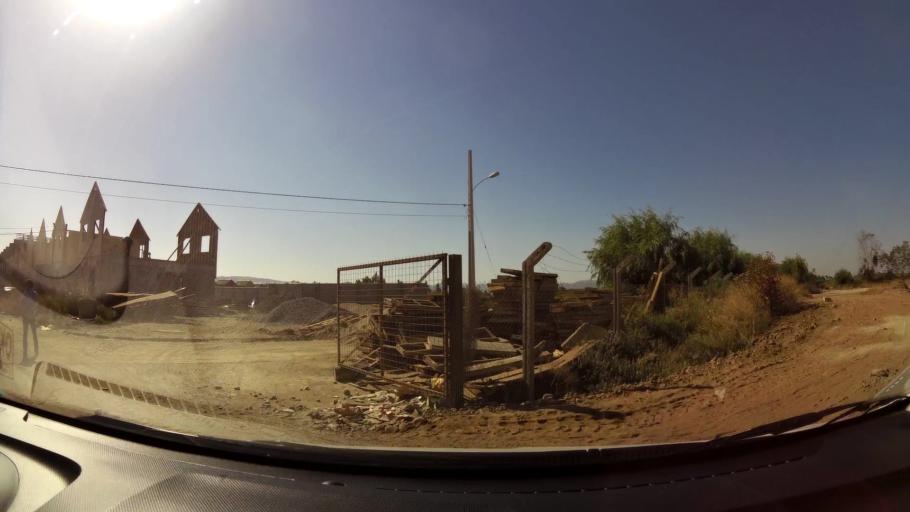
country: CL
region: Maule
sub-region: Provincia de Talca
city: Talca
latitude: -35.4155
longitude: -71.6014
